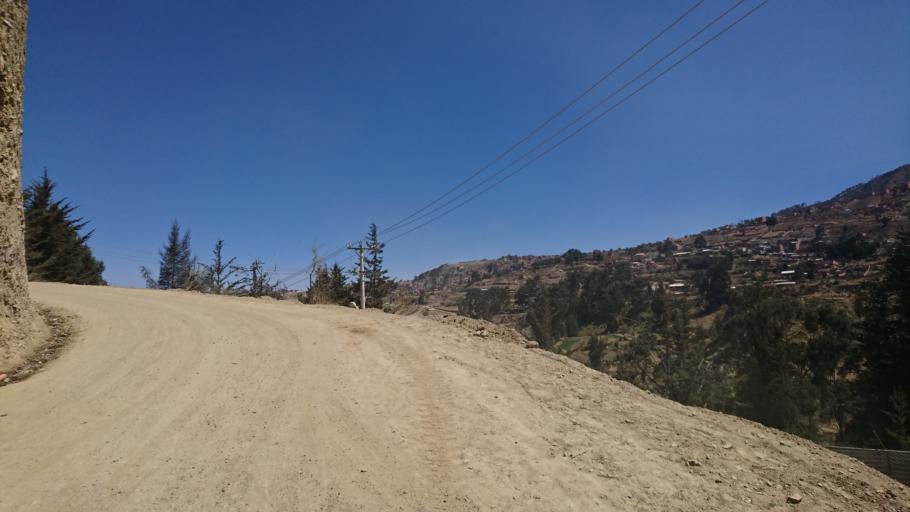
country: BO
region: La Paz
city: La Paz
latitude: -16.4887
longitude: -68.0806
